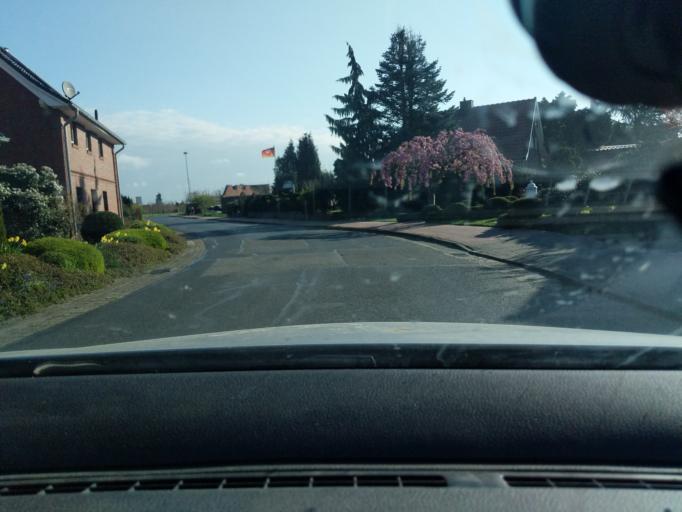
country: DE
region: Lower Saxony
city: Grunendeich
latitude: 53.5653
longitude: 9.6370
